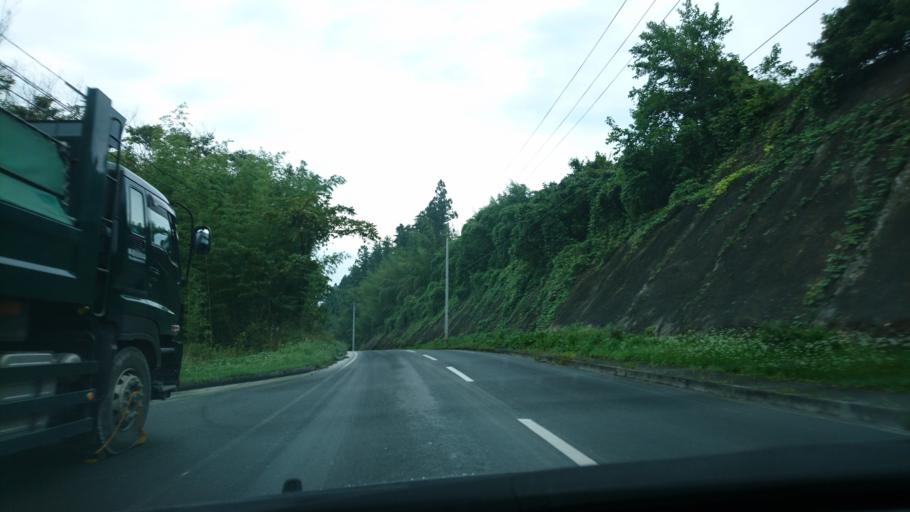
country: JP
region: Iwate
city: Ichinoseki
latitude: 38.9663
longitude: 141.2448
